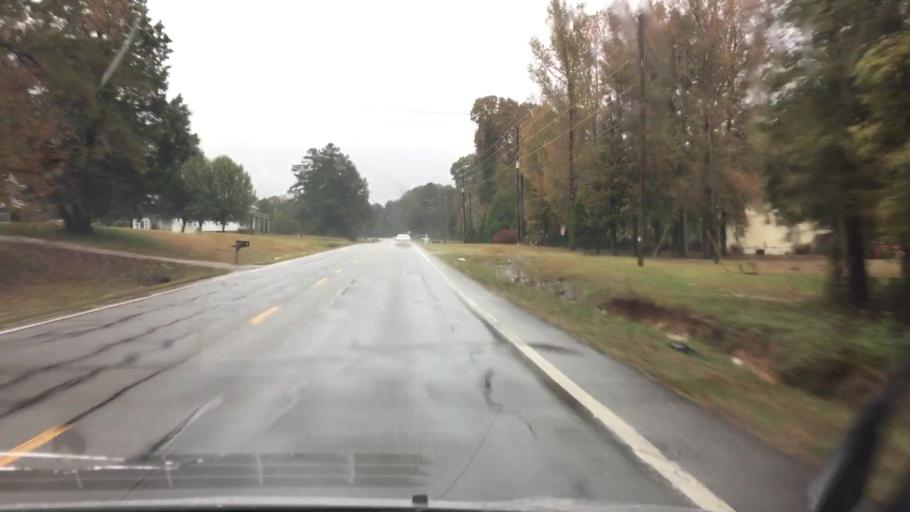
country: US
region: Georgia
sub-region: Henry County
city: Stockbridge
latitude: 33.5581
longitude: -84.1374
